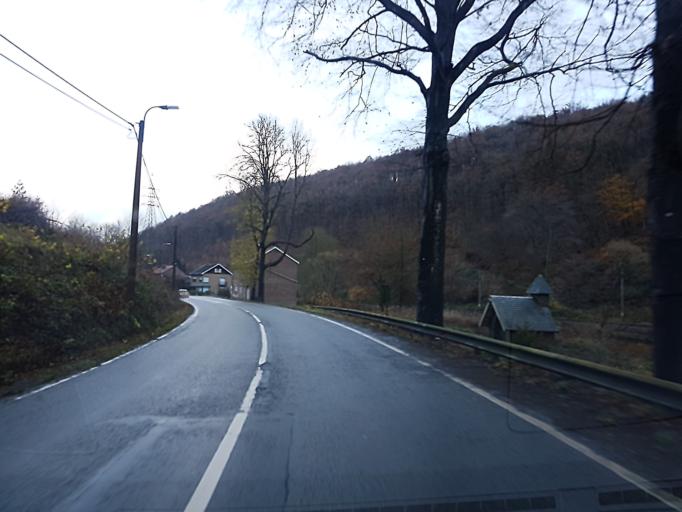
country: BE
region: Wallonia
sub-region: Province de Liege
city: Theux
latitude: 50.5011
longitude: 5.8312
